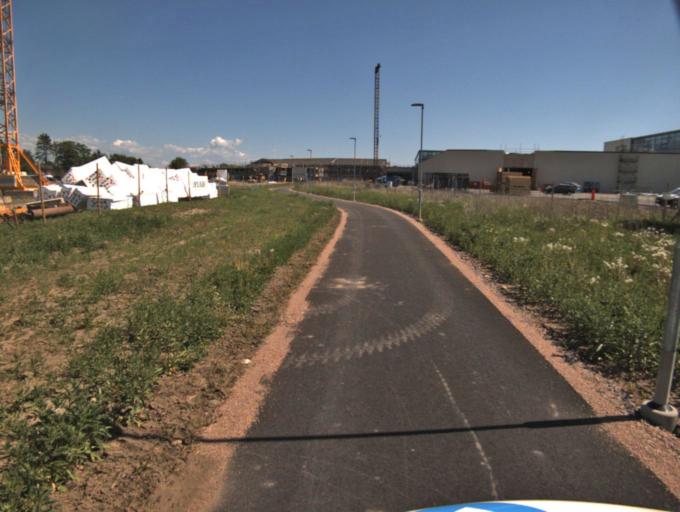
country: SE
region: Skane
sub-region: Kristianstads Kommun
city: Kristianstad
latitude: 56.0268
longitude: 14.2027
